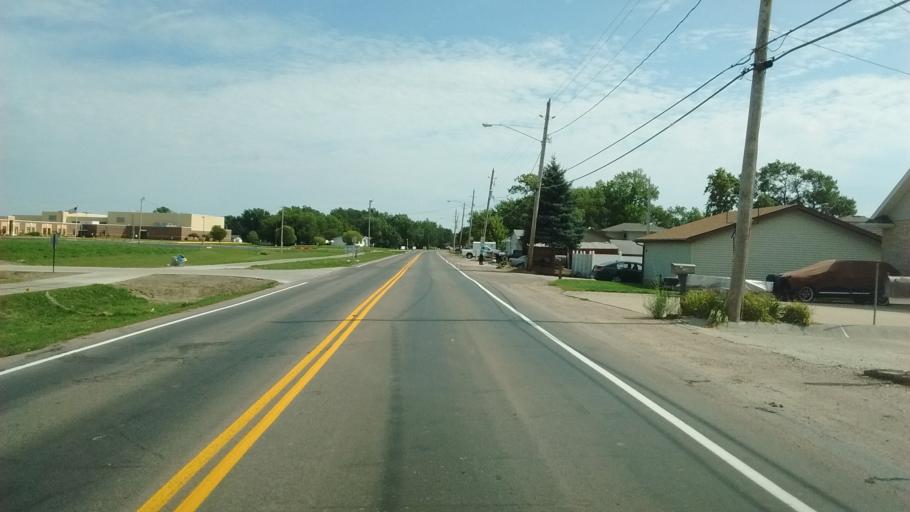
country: US
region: South Dakota
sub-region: Union County
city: North Sioux City
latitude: 42.5492
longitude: -96.5211
